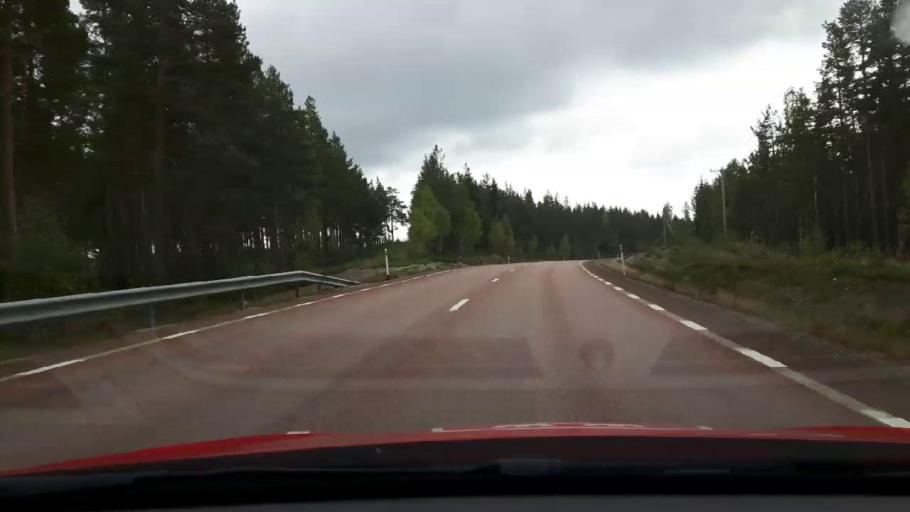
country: SE
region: Gaevleborg
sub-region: Soderhamns Kommun
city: Soderhamn
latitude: 61.1241
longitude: 16.9331
